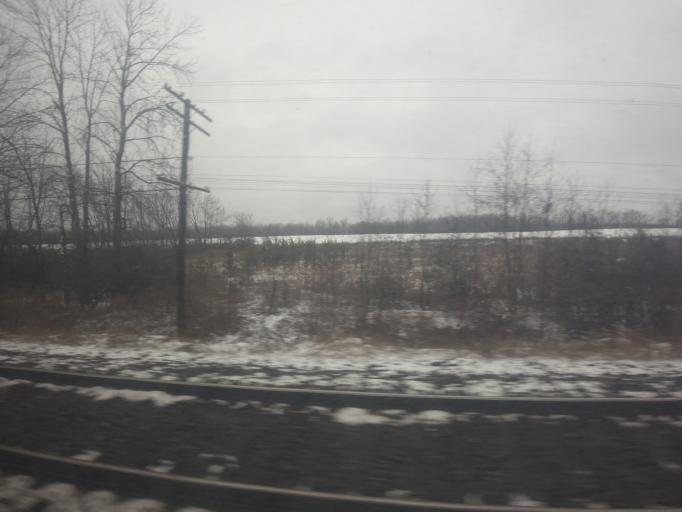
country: CA
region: Ontario
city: Quinte West
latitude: 44.1392
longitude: -77.5247
